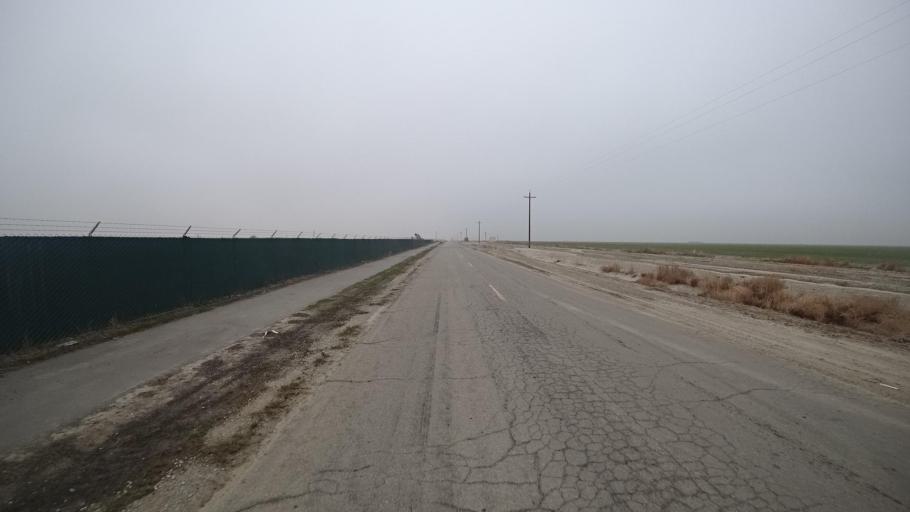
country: US
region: California
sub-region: Kern County
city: Rosedale
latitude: 35.2399
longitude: -119.2528
